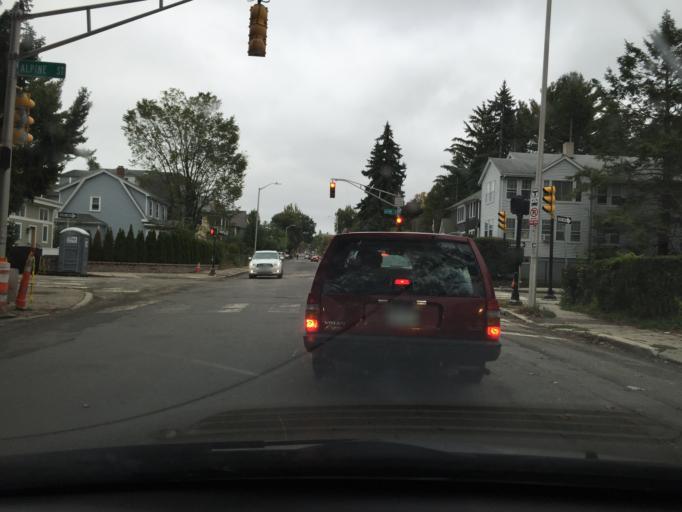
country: US
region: Massachusetts
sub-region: Middlesex County
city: Cambridge
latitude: 42.3853
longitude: -71.1376
